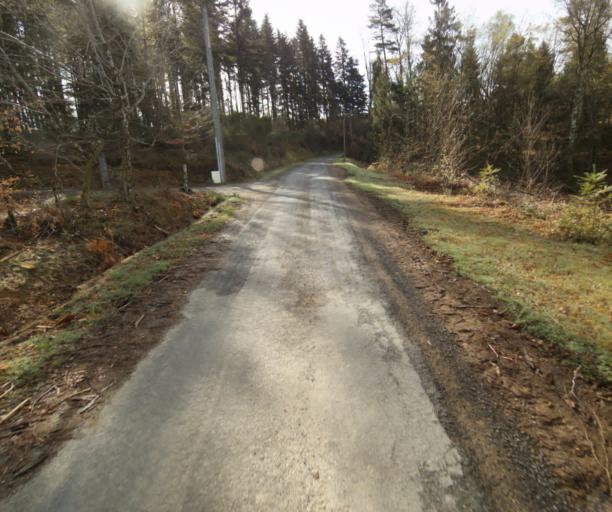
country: FR
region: Limousin
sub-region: Departement de la Correze
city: Laguenne
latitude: 45.2826
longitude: 1.8299
